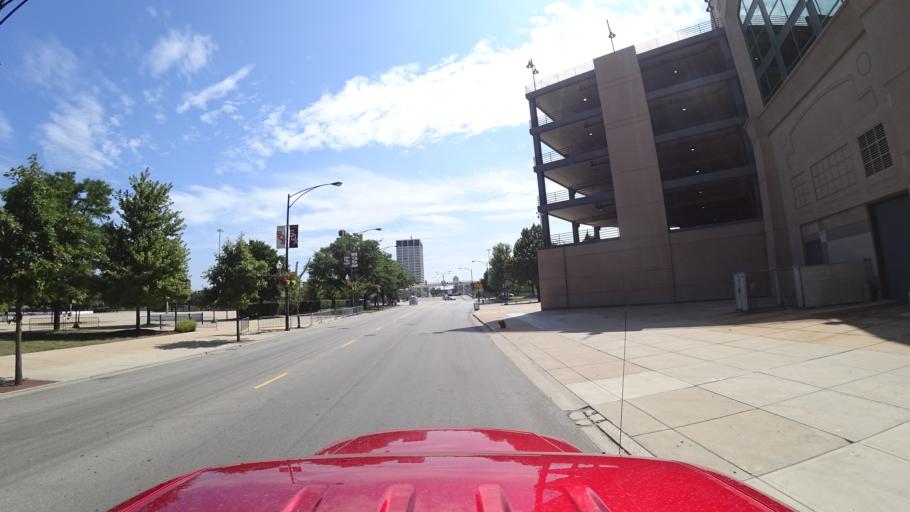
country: US
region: Illinois
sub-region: Cook County
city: Chicago
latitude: 41.8309
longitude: -87.6331
